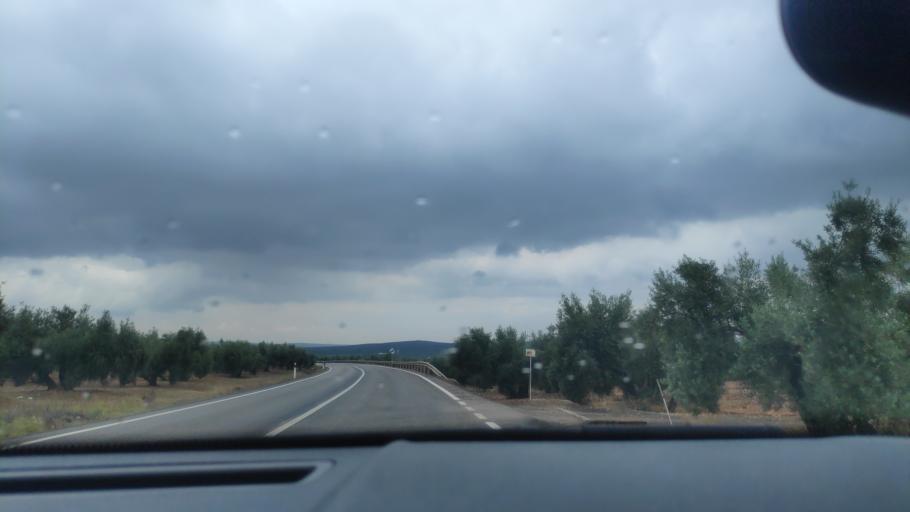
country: ES
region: Andalusia
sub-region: Provincia de Jaen
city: Jabalquinto
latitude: 38.0388
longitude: -3.7470
